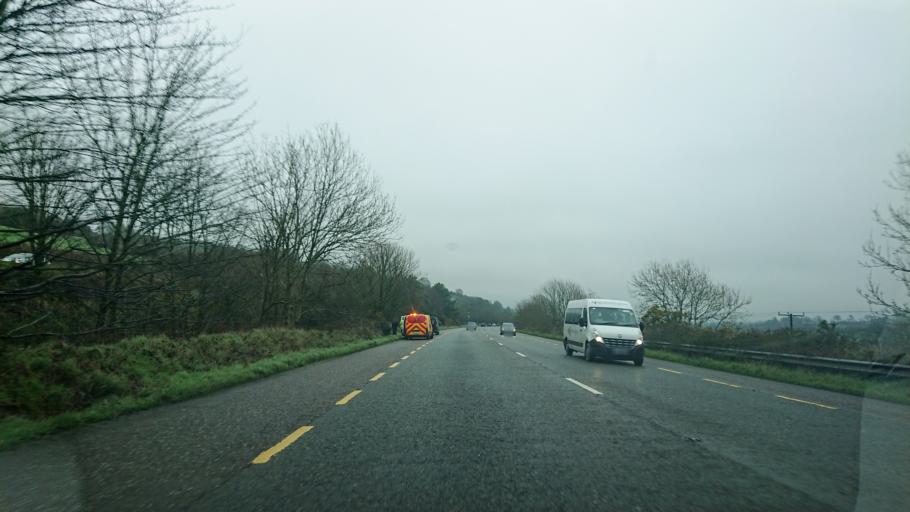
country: IE
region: Munster
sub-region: County Cork
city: Kinsale
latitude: 51.8062
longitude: -8.5632
